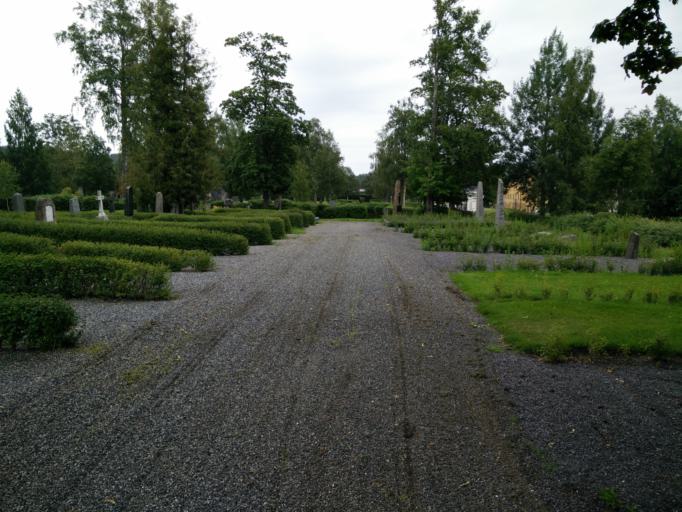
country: SE
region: Vaesternorrland
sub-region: Haernoesands Kommun
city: Haernoesand
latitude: 62.6292
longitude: 17.9511
